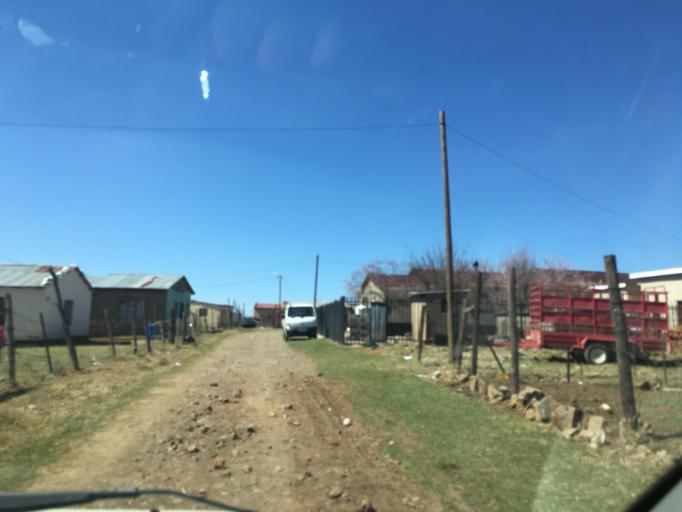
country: ZA
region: Eastern Cape
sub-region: Chris Hani District Municipality
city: Elliot
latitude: -31.3299
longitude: 27.8218
